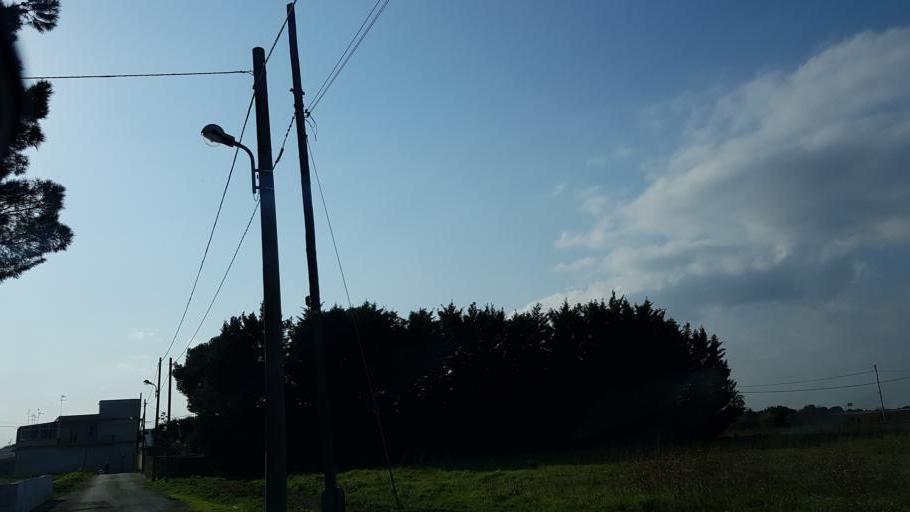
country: IT
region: Apulia
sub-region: Provincia di Brindisi
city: Mesagne
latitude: 40.5666
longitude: 17.8049
